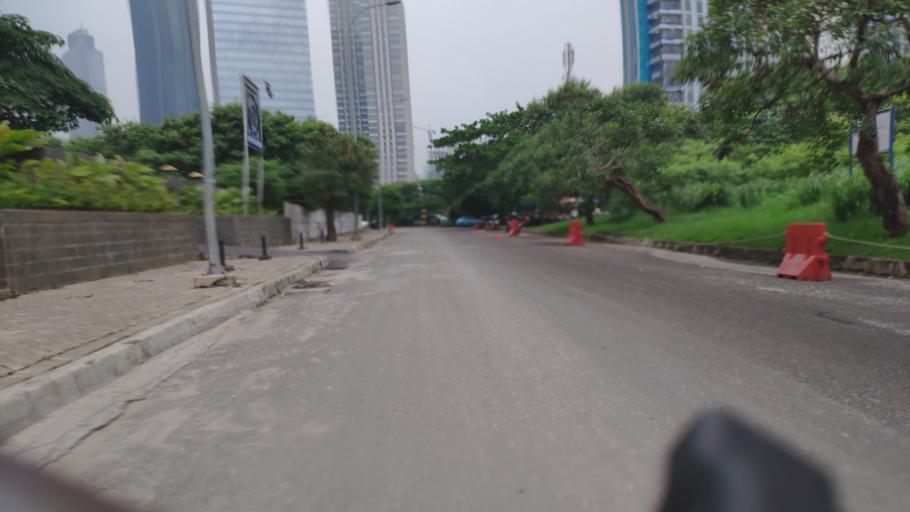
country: ID
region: Jakarta Raya
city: Jakarta
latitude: -6.2137
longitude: 106.8369
